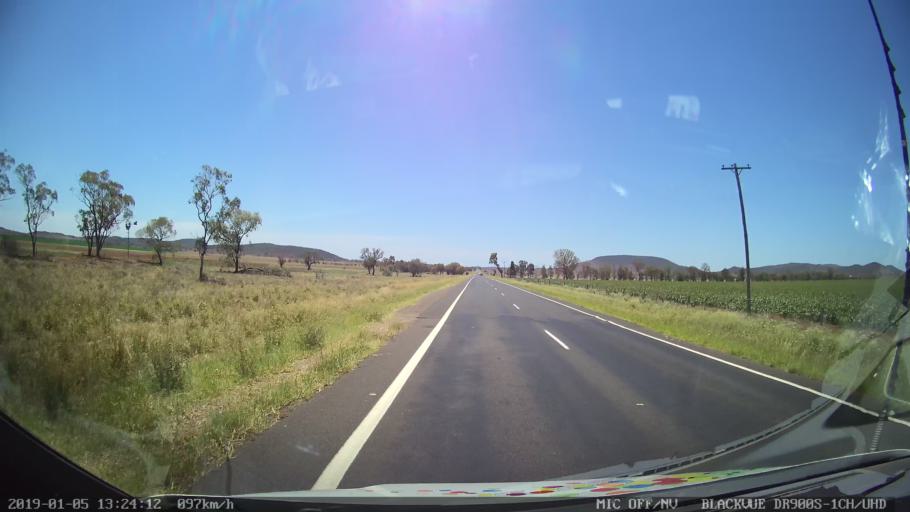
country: AU
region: New South Wales
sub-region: Gunnedah
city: Gunnedah
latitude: -31.0714
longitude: 149.9857
